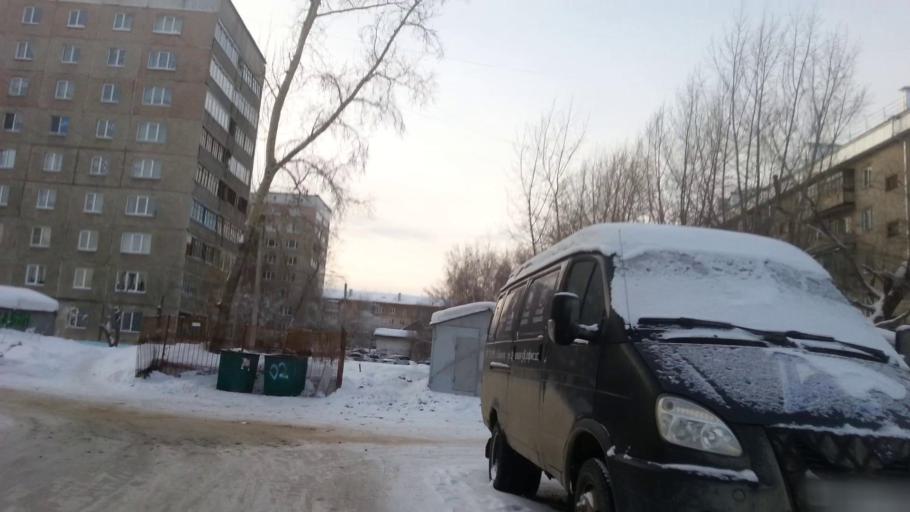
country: RU
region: Altai Krai
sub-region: Gorod Barnaulskiy
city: Barnaul
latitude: 53.3538
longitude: 83.6896
